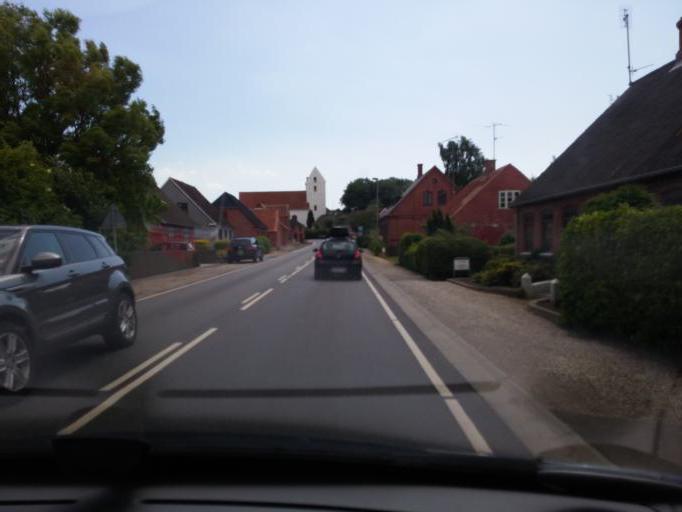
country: DK
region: South Denmark
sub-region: Langeland Kommune
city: Rudkobing
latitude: 54.8667
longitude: 10.7300
